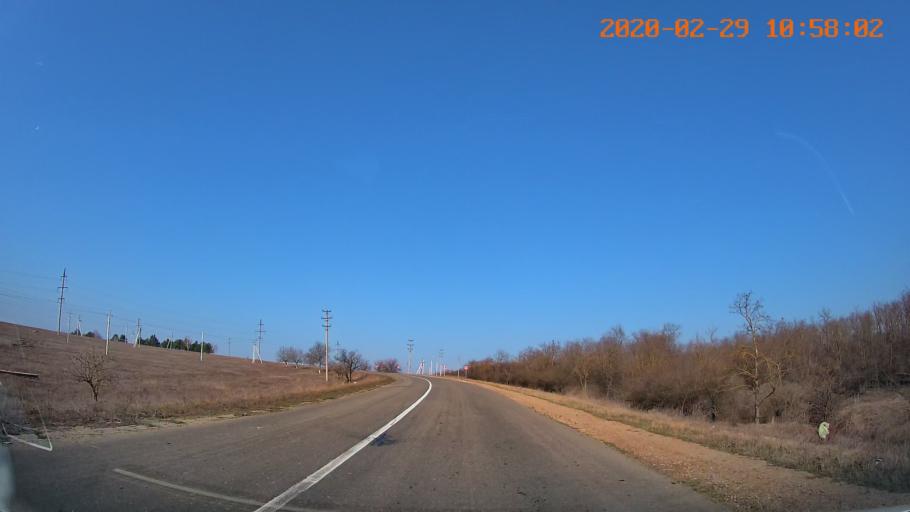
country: MD
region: Telenesti
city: Grigoriopol
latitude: 47.1661
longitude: 29.3176
